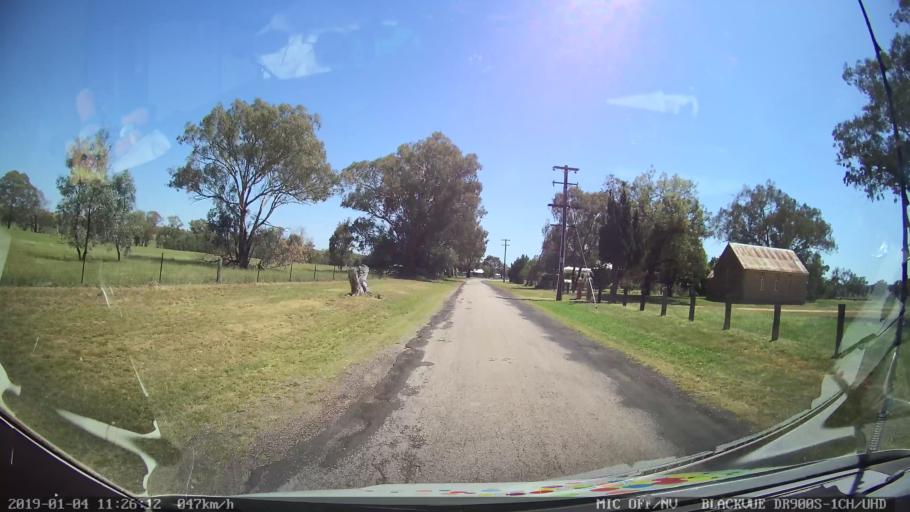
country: AU
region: New South Wales
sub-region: Cabonne
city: Molong
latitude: -33.1169
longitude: 148.7555
